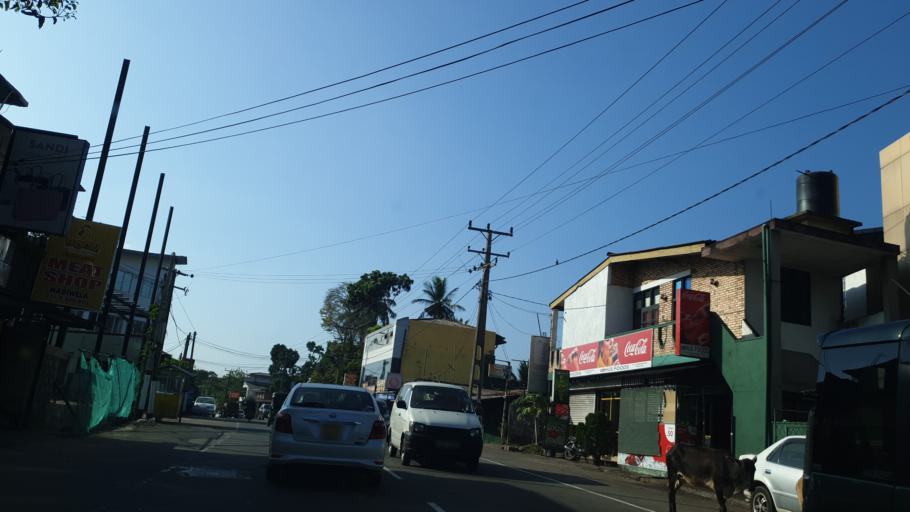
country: LK
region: Western
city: Sri Jayewardenepura Kotte
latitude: 6.8777
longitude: 79.9249
